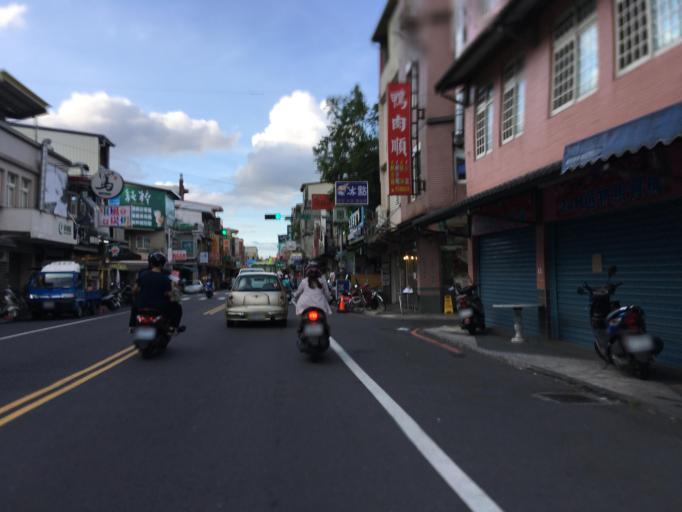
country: TW
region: Taiwan
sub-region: Yilan
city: Yilan
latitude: 24.6662
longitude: 121.7677
